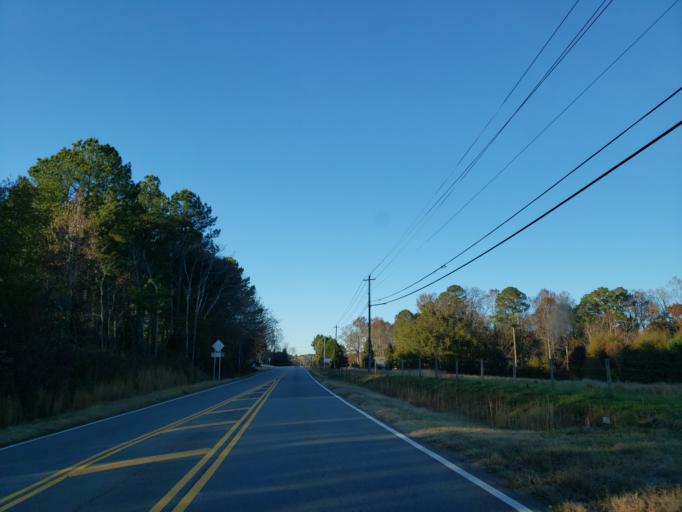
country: US
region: Georgia
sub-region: Cherokee County
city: Holly Springs
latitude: 34.1800
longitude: -84.4198
